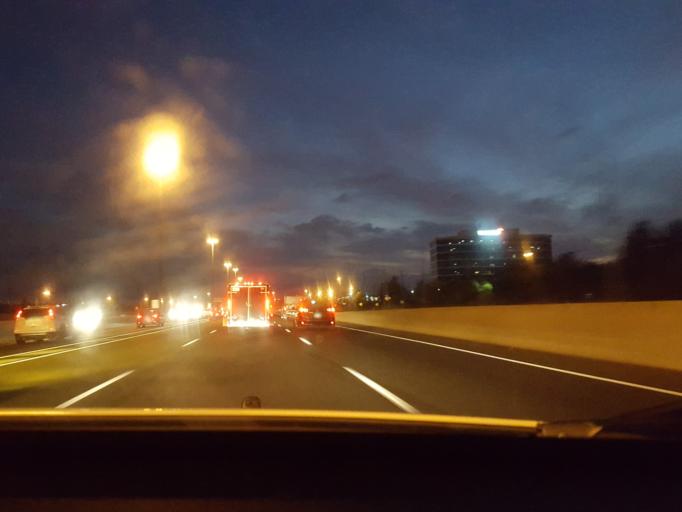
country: CA
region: Ontario
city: Oakville
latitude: 43.4336
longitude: -79.7148
